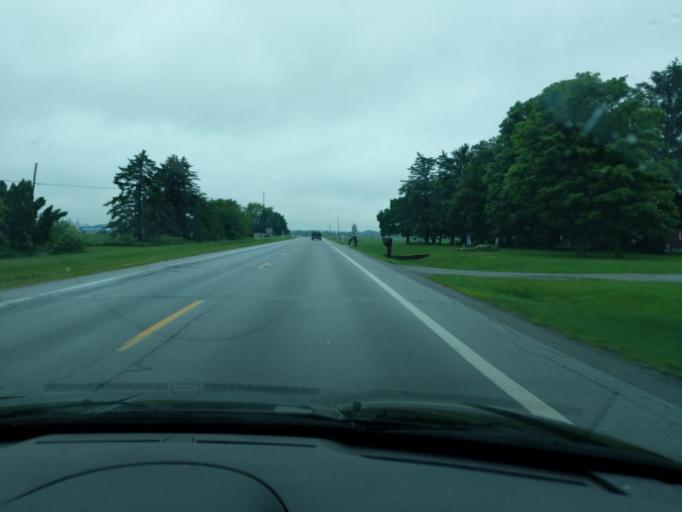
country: US
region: Ohio
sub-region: Logan County
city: West Liberty
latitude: 40.2334
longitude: -83.7518
